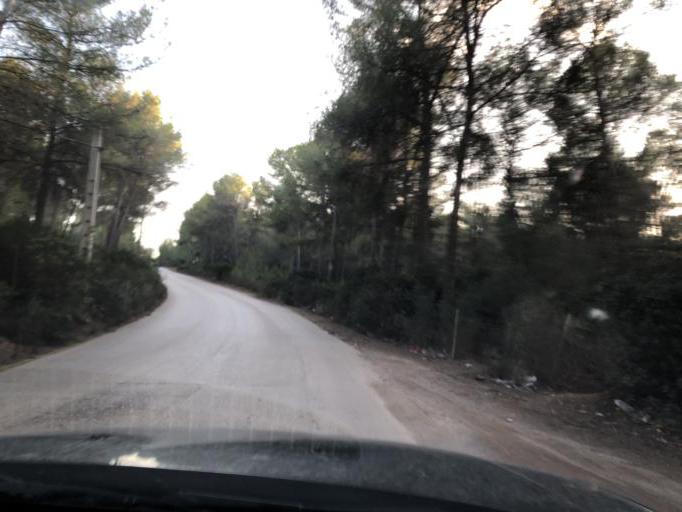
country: ES
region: Balearic Islands
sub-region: Illes Balears
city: Santa Ponsa
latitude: 39.5377
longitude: 2.4819
